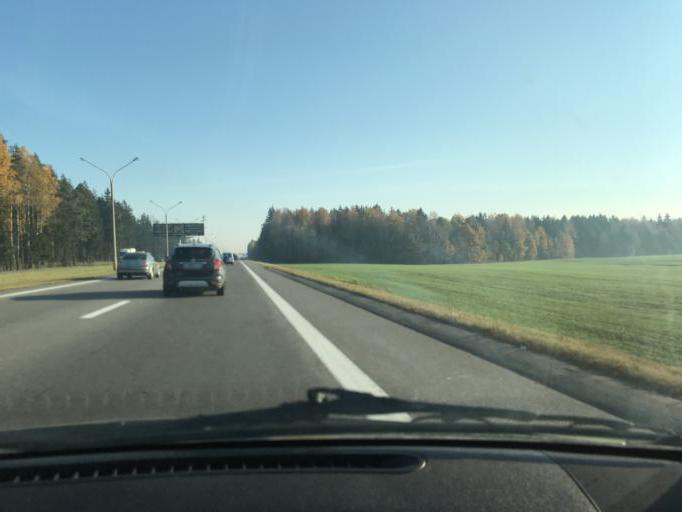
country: BY
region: Minsk
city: Korolev Stan
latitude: 54.0019
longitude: 27.8357
